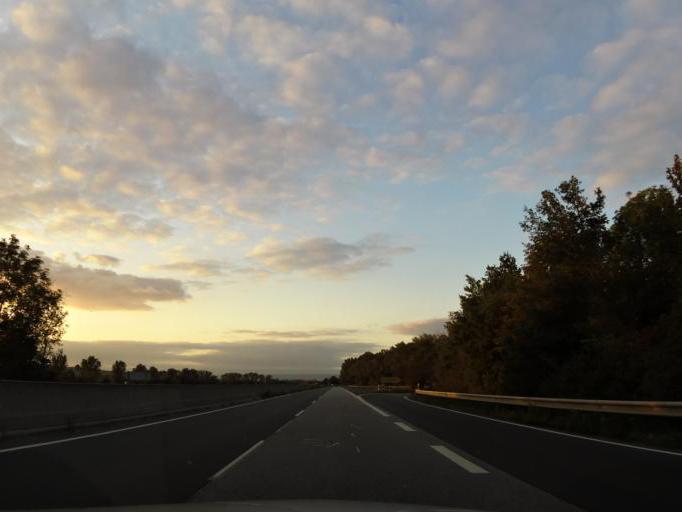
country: DE
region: Rheinland-Pfalz
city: Nackenheim
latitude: 49.9309
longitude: 8.3423
